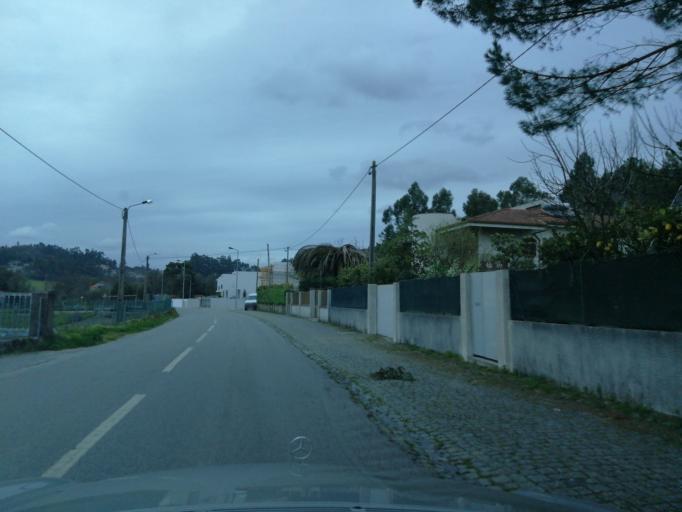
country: PT
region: Braga
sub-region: Braga
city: Oliveira
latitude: 41.4807
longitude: -8.4713
